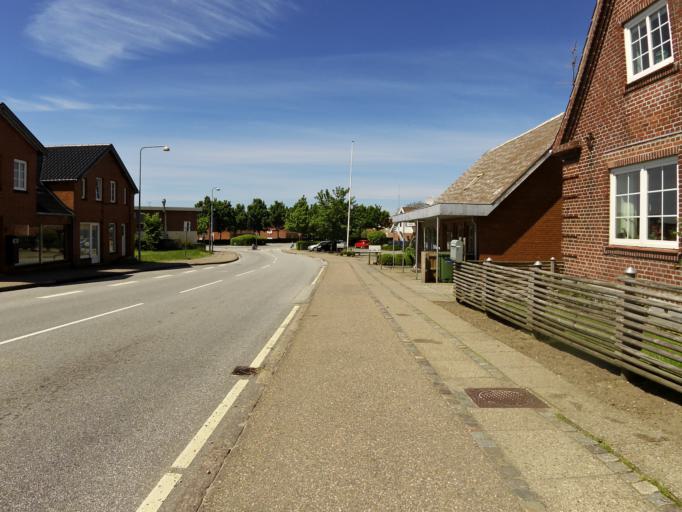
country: DK
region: South Denmark
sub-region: Haderslev Kommune
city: Gram
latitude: 55.2873
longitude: 9.0509
